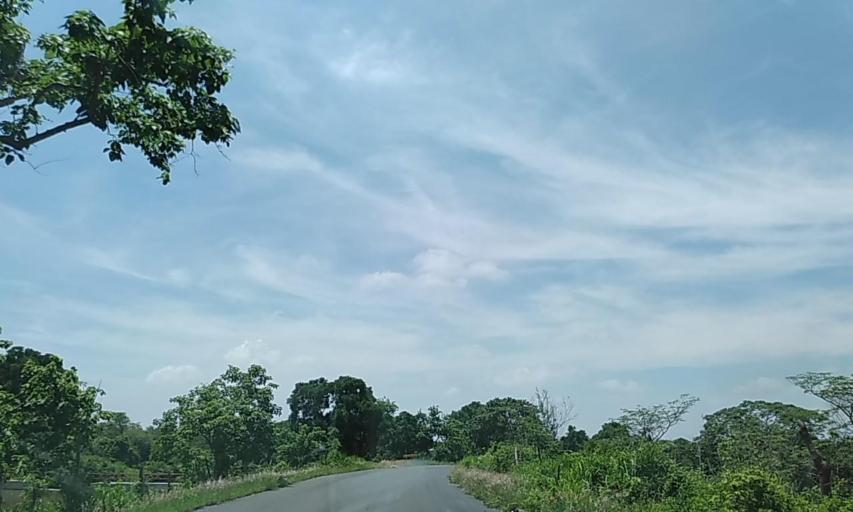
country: MX
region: Veracruz
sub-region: Emiliano Zapata
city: Dos Rios
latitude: 19.4423
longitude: -96.7590
